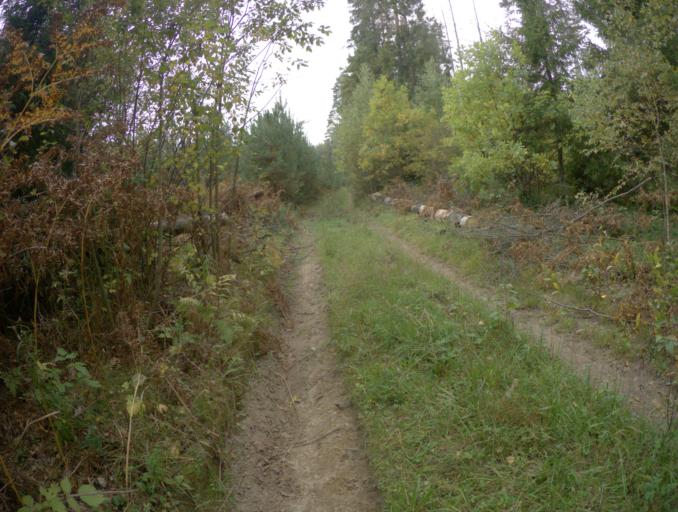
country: RU
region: Vladimir
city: Golovino
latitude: 55.9908
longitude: 40.4674
